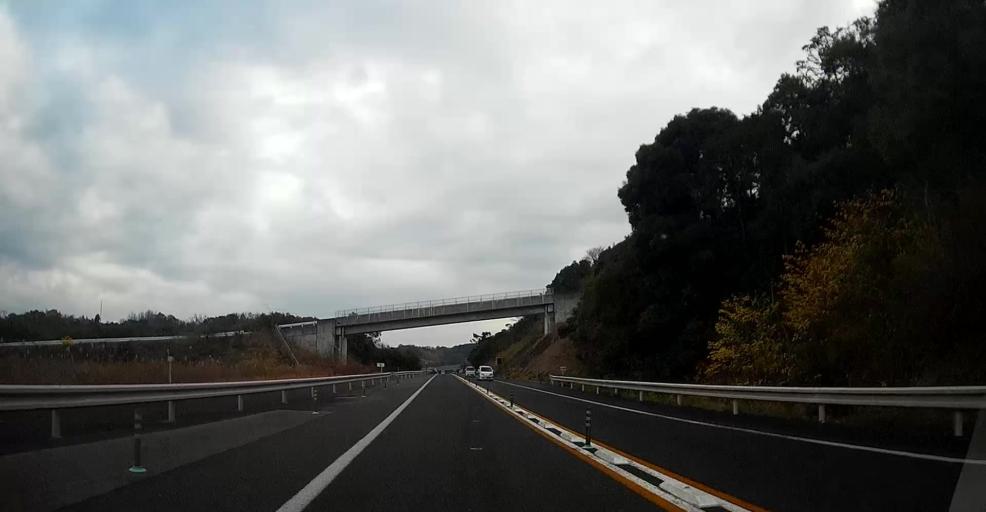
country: JP
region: Kumamoto
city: Hondo
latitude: 32.5095
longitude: 130.3254
